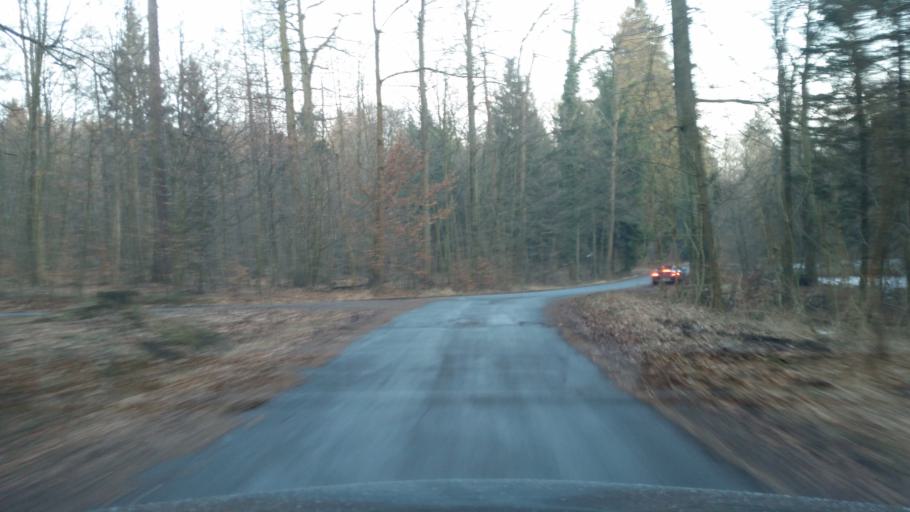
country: DE
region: Lower Saxony
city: Hameln
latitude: 52.0929
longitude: 9.3127
